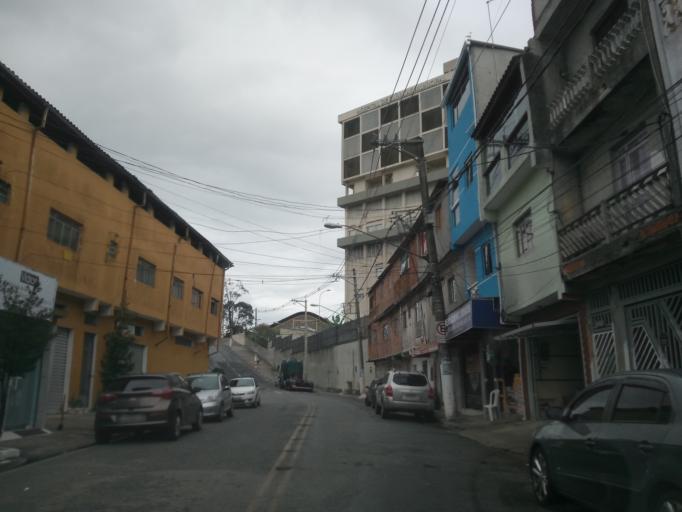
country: BR
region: Sao Paulo
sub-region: Sao Bernardo Do Campo
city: Sao Bernardo do Campo
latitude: -23.7330
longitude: -46.5767
